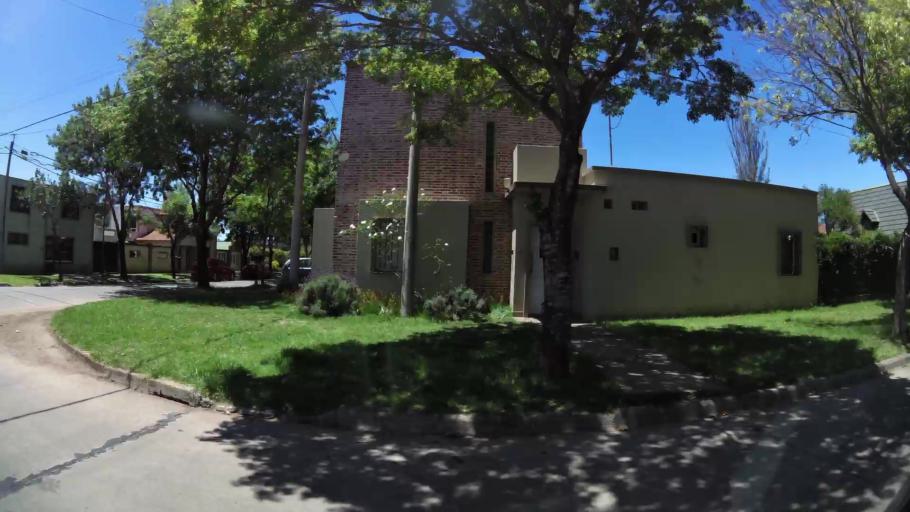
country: AR
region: Santa Fe
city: Rafaela
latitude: -31.2552
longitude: -61.4619
